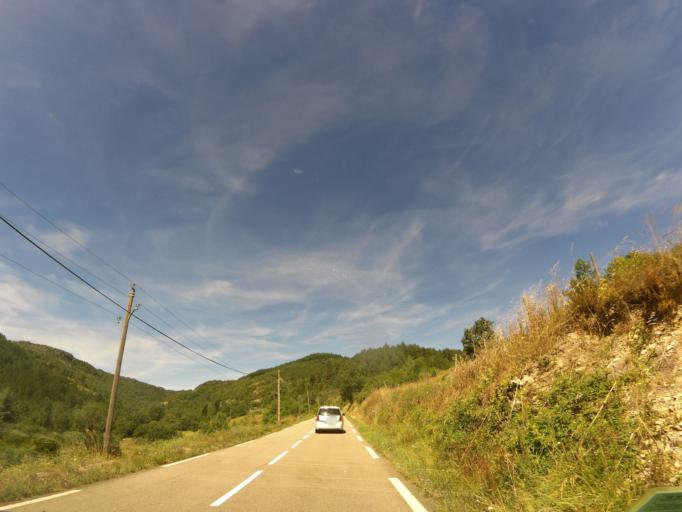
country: FR
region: Languedoc-Roussillon
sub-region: Departement du Gard
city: Le Vigan
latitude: 43.9642
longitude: 3.4350
